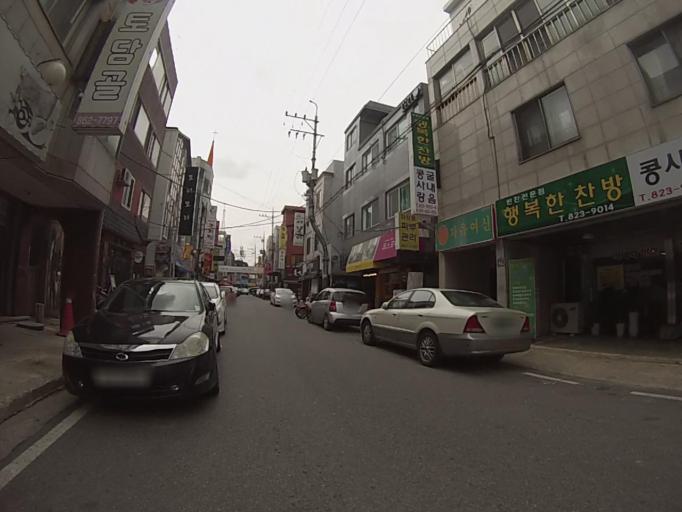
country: KR
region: Daejeon
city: Songgang-dong
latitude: 36.3635
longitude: 127.3579
